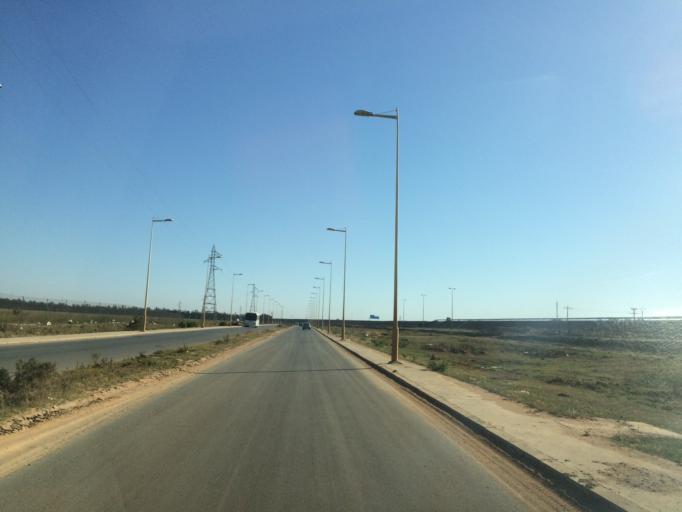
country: MA
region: Rabat-Sale-Zemmour-Zaer
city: Sale
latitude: 33.9870
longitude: -6.7286
